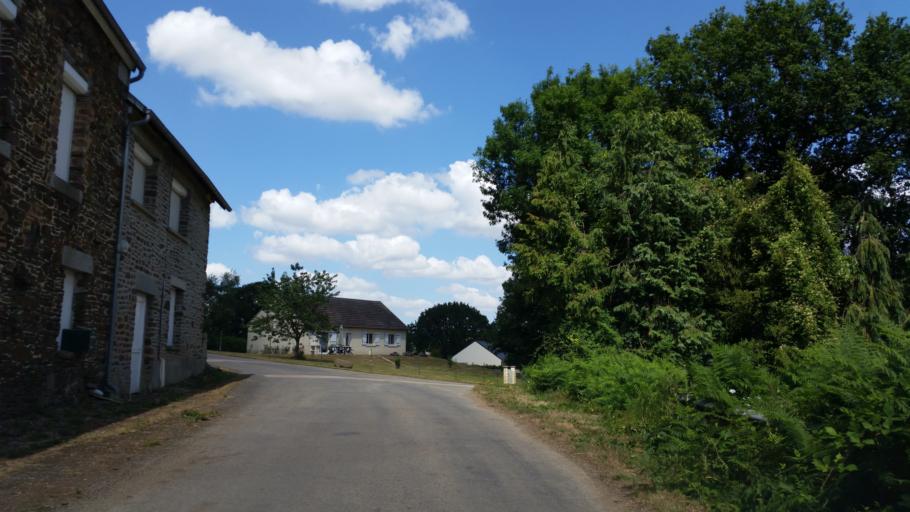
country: FR
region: Lower Normandy
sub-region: Departement du Calvados
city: Clecy
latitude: 48.8404
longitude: -0.3763
